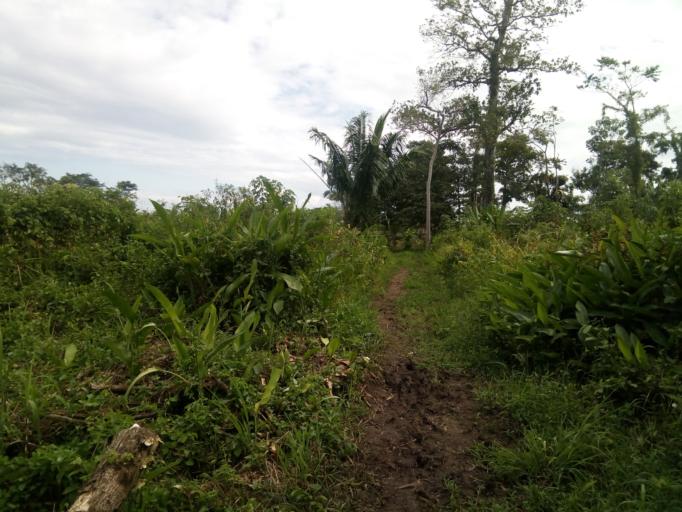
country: CR
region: Alajuela
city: San Jose
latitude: 11.0577
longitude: -85.1972
